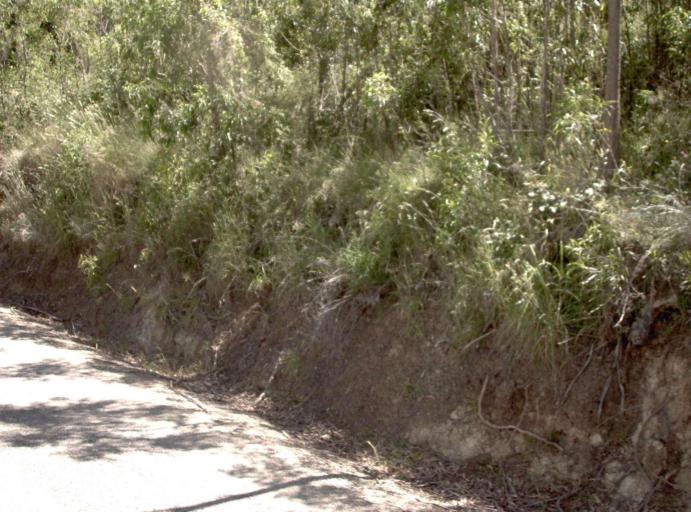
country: AU
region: Victoria
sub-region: East Gippsland
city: Lakes Entrance
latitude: -37.4584
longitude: 148.1962
